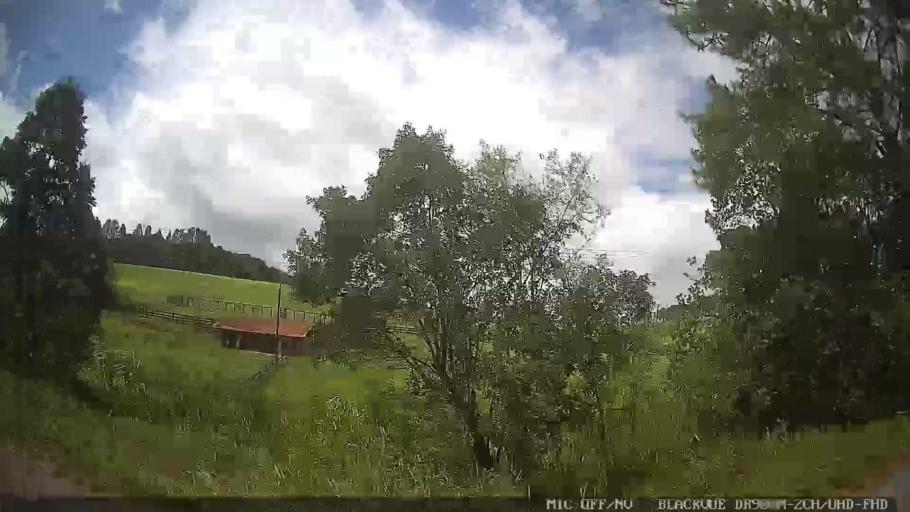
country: BR
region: Sao Paulo
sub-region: Braganca Paulista
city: Braganca Paulista
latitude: -22.8028
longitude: -46.4989
